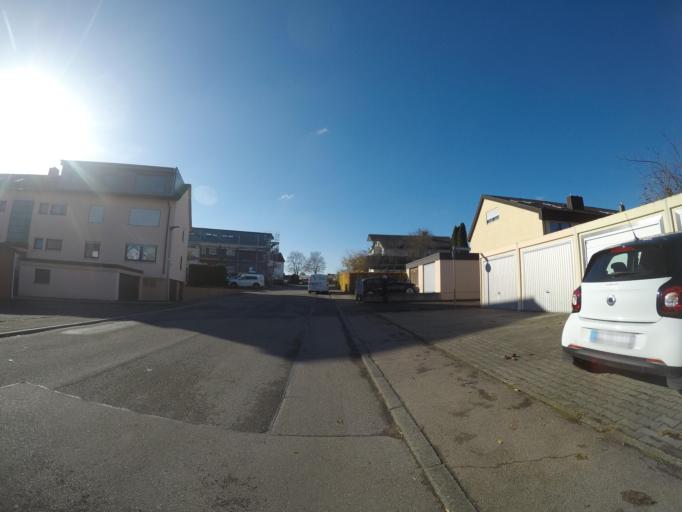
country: DE
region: Baden-Wuerttemberg
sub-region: Tuebingen Region
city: Dornstadt
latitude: 48.4703
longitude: 9.9355
